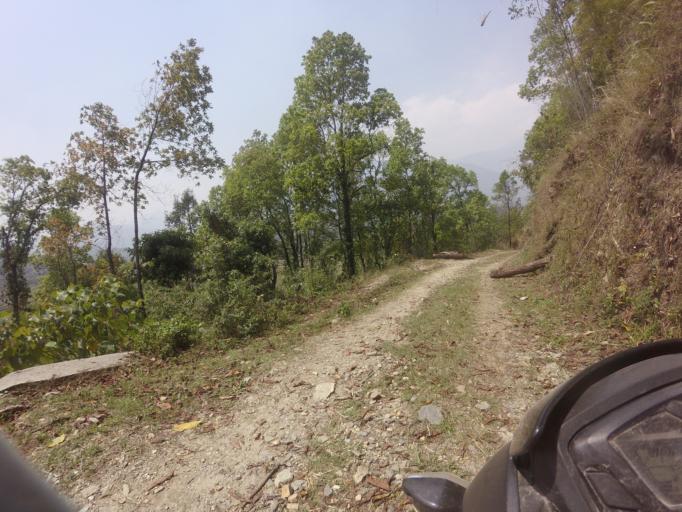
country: NP
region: Western Region
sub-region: Gandaki Zone
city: Pokhara
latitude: 28.3023
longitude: 83.9654
